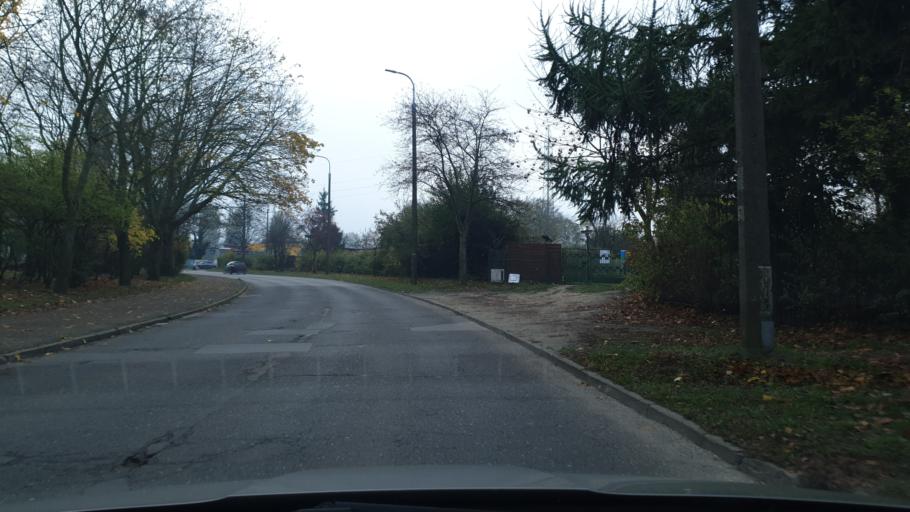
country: PL
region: Pomeranian Voivodeship
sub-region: Sopot
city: Sopot
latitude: 54.3962
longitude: 18.5871
